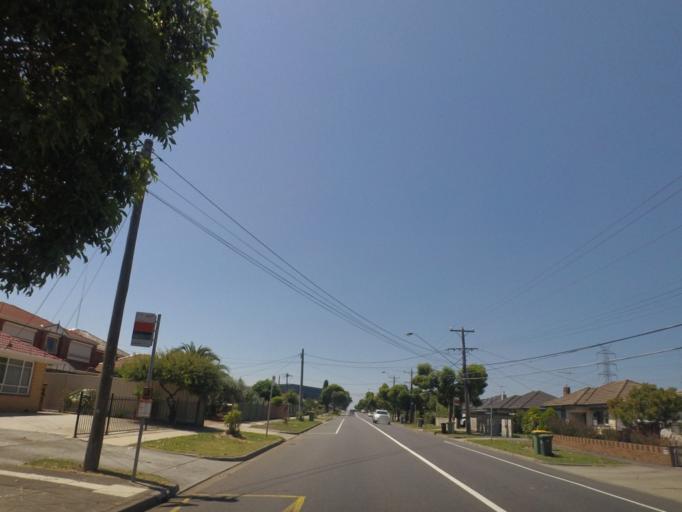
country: AU
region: Victoria
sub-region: Darebin
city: Reservoir
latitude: -37.7127
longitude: 144.9894
